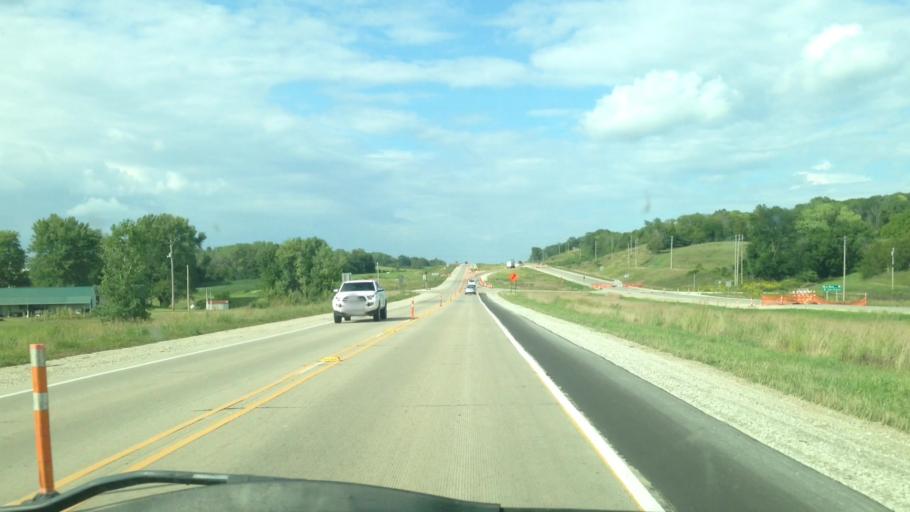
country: US
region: Iowa
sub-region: Henry County
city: Mount Pleasant
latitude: 40.8997
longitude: -91.5550
